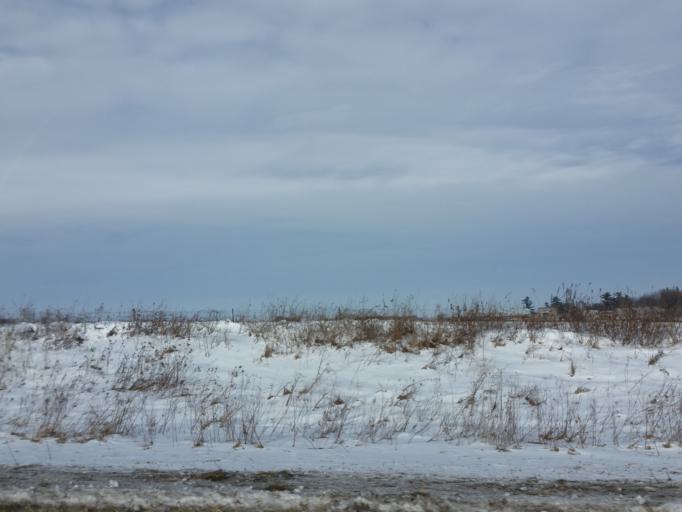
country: US
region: Iowa
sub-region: Buchanan County
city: Independence
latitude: 42.4617
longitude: -91.7418
